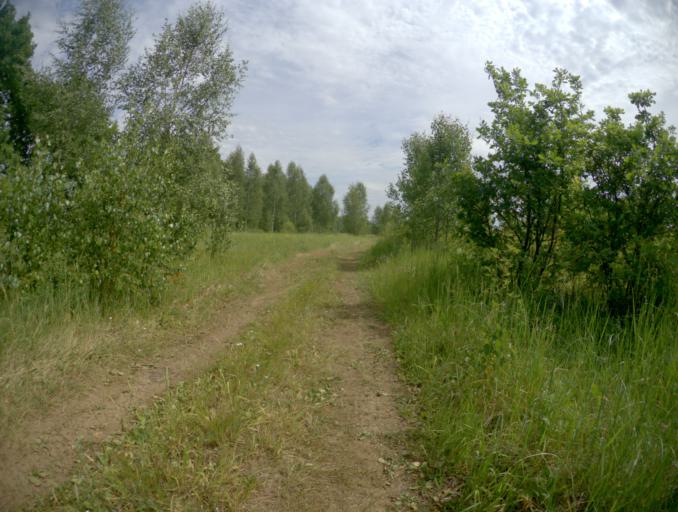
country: RU
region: Vladimir
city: Raduzhnyy
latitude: 56.0309
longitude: 40.2557
